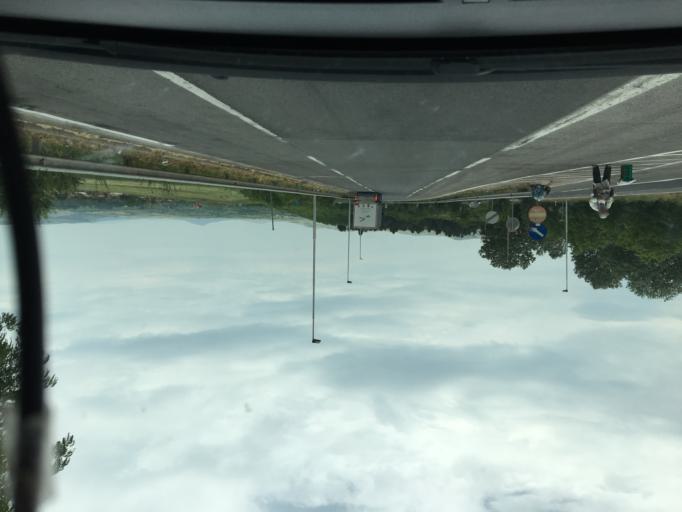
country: MK
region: Gradsko
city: Gradsko
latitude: 41.5740
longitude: 21.9352
